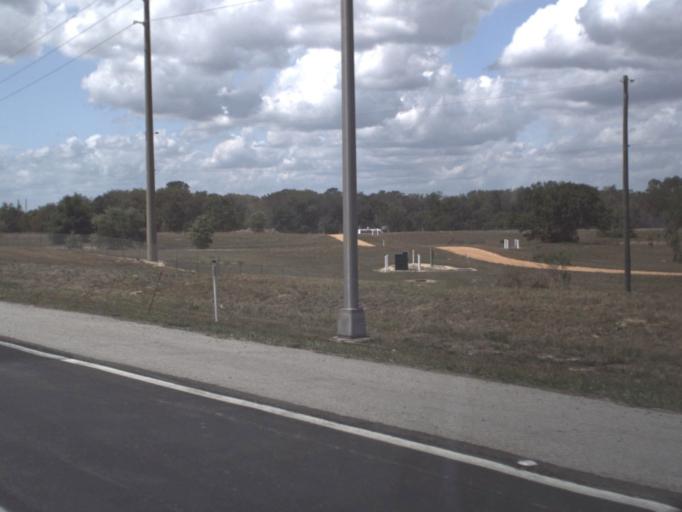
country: US
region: Florida
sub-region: Orange County
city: Oakland
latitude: 28.4945
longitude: -81.6209
